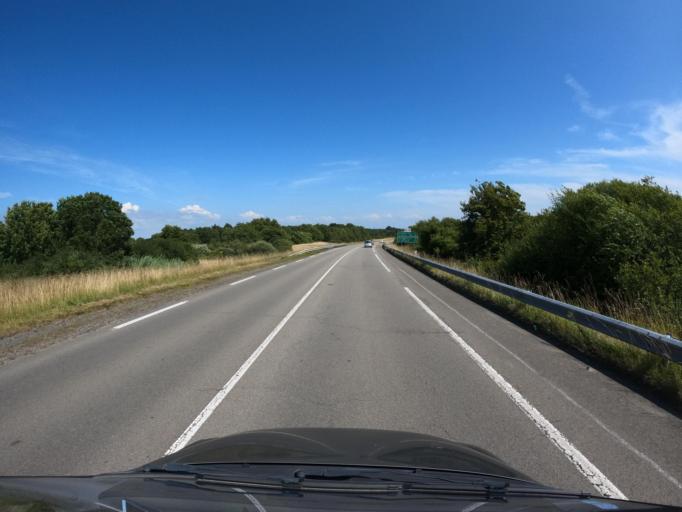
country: FR
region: Pays de la Loire
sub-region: Departement de la Loire-Atlantique
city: La Bernerie-en-Retz
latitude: 47.1031
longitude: -2.0436
